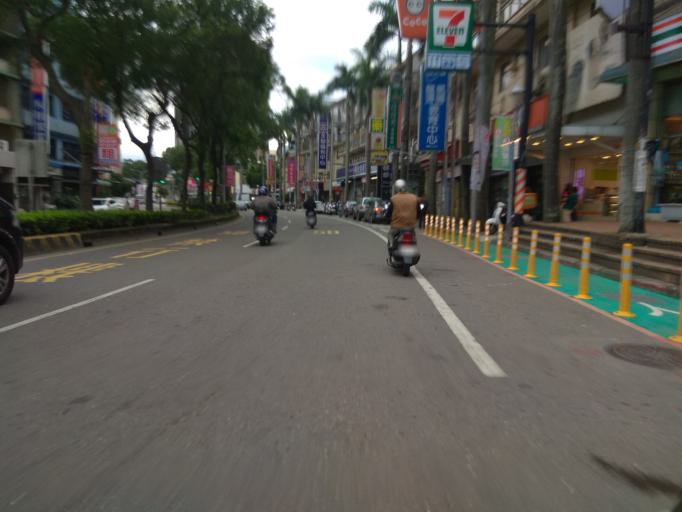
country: TW
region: Taiwan
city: Daxi
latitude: 24.8786
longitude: 121.2116
